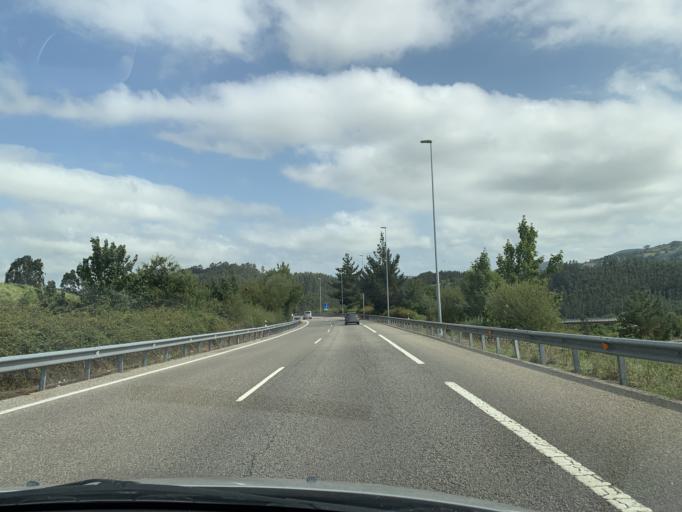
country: ES
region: Asturias
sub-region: Province of Asturias
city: Villaviciosa
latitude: 43.4659
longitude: -5.4925
